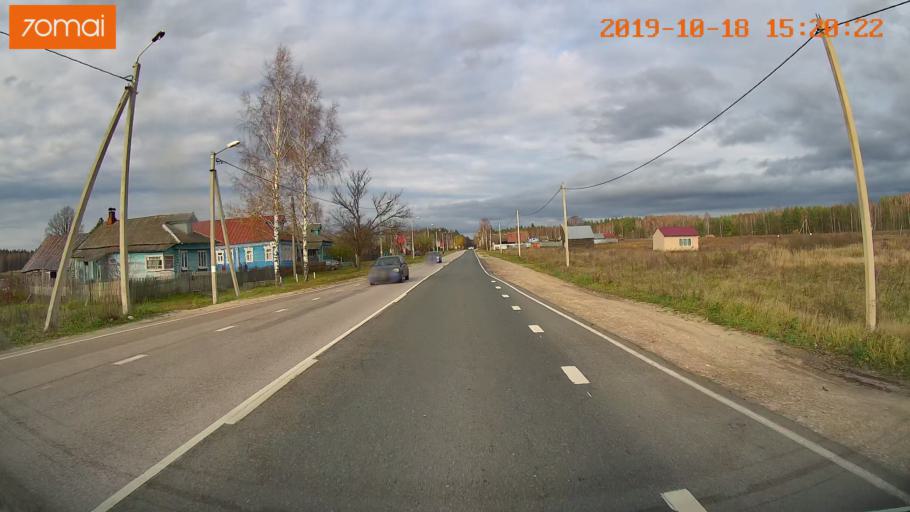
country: RU
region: Vladimir
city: Anopino
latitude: 55.6861
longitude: 40.7442
